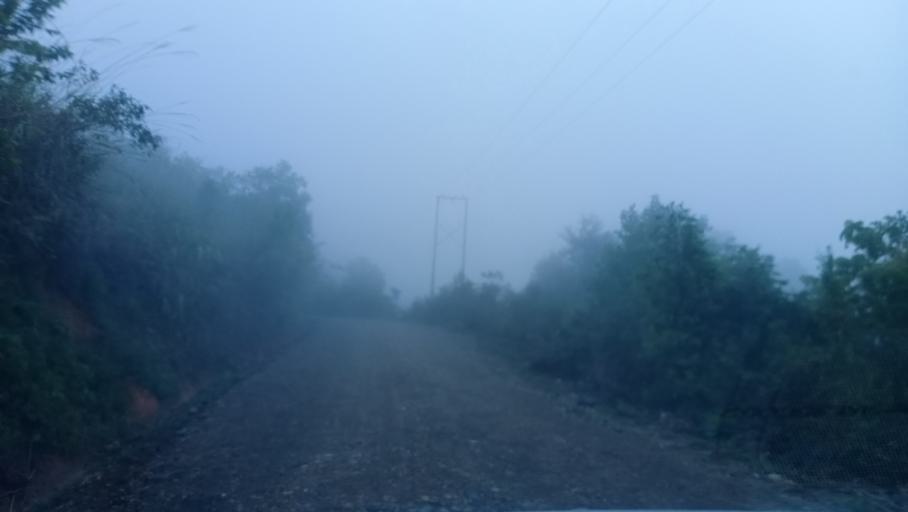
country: LA
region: Phongsali
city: Phongsali
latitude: 21.5100
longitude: 102.1736
